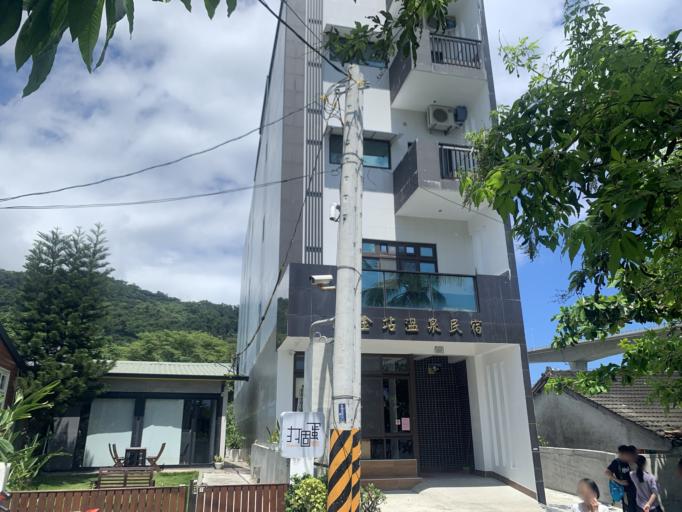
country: TW
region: Taiwan
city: Taitung City
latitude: 22.5312
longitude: 120.9663
